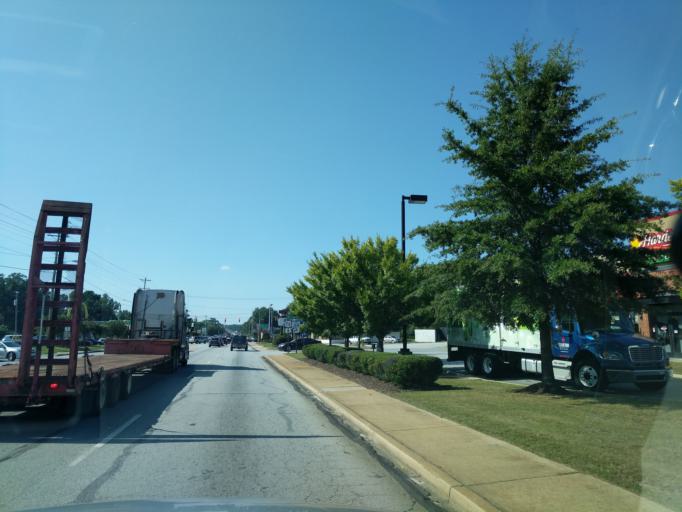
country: US
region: South Carolina
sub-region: Newberry County
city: Newberry
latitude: 34.2837
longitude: -81.5969
